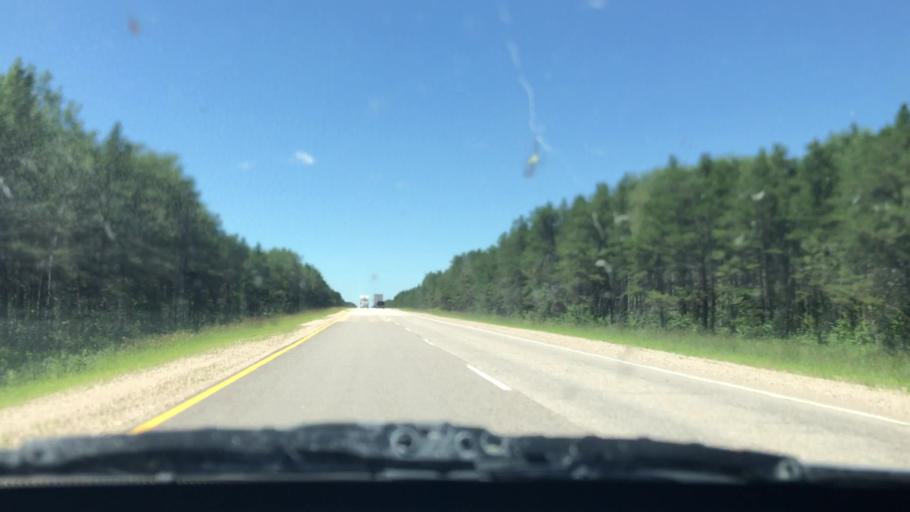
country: CA
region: Manitoba
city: La Broquerie
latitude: 49.6564
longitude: -96.1756
